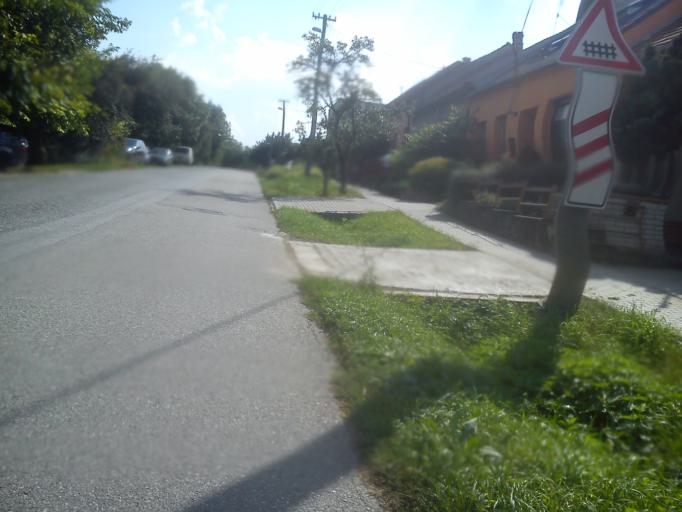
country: CZ
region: South Moravian
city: Sokolnice
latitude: 49.1107
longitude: 16.7294
